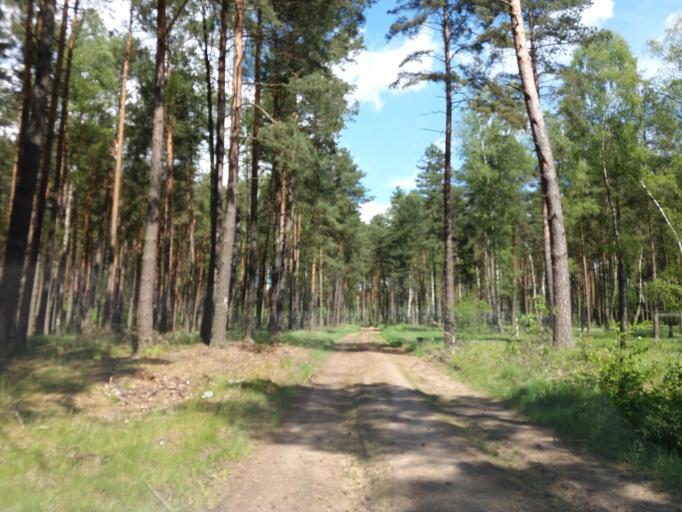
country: PL
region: West Pomeranian Voivodeship
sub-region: Powiat choszczenski
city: Drawno
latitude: 53.2663
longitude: 15.7334
